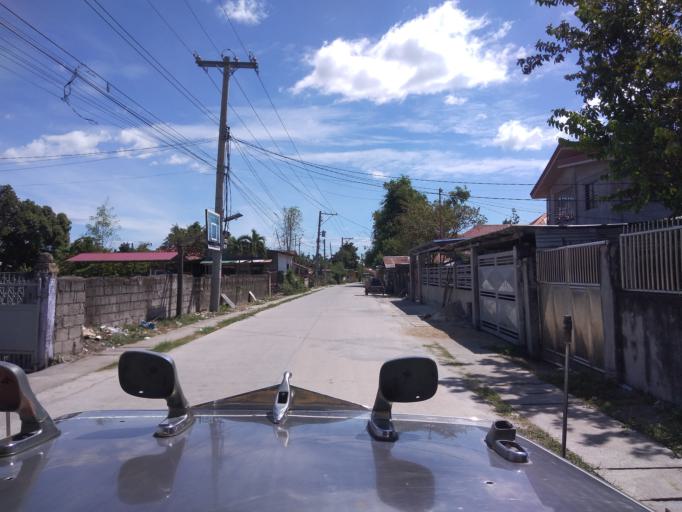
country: PH
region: Central Luzon
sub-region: Province of Pampanga
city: Magliman
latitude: 15.0430
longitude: 120.6440
